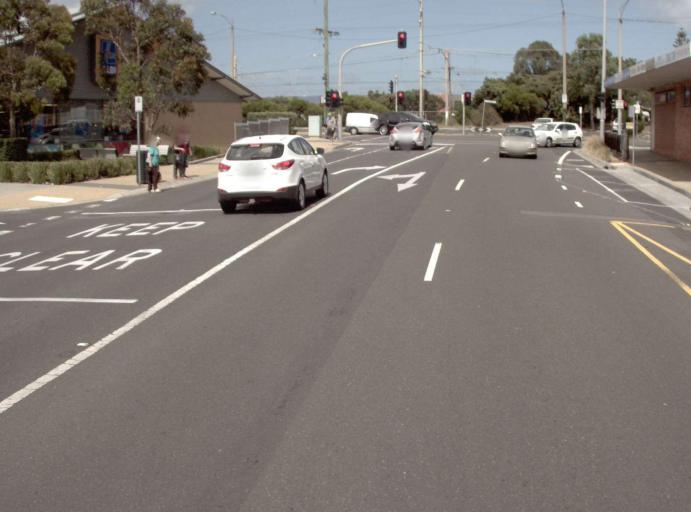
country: AU
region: Victoria
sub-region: Kingston
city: Bonbeach
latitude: -38.0761
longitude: 145.1238
